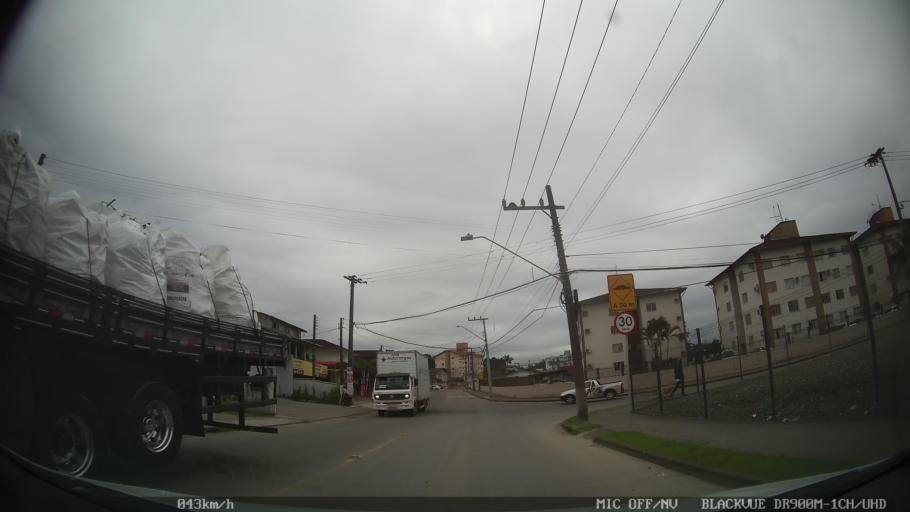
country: BR
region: Santa Catarina
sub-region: Joinville
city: Joinville
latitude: -26.2691
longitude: -48.8910
